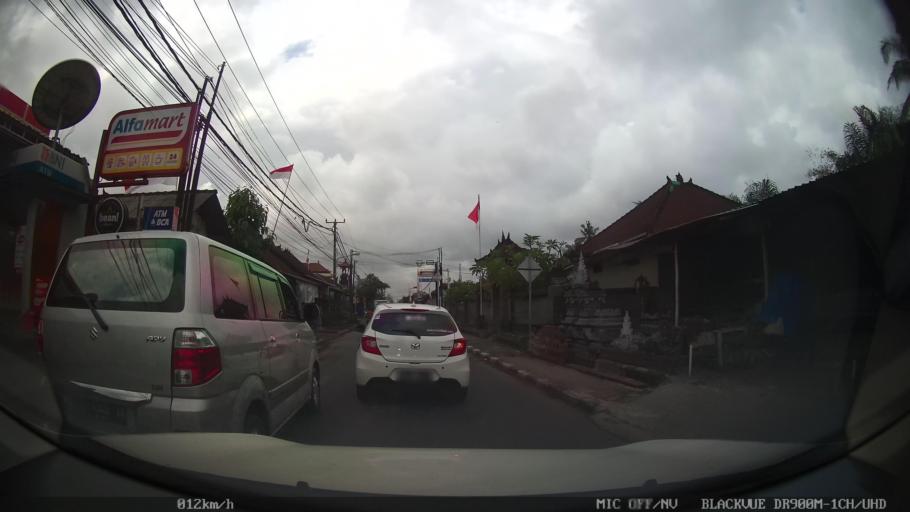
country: ID
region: Bali
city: Banjar Bucu
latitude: -8.5867
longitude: 115.2117
